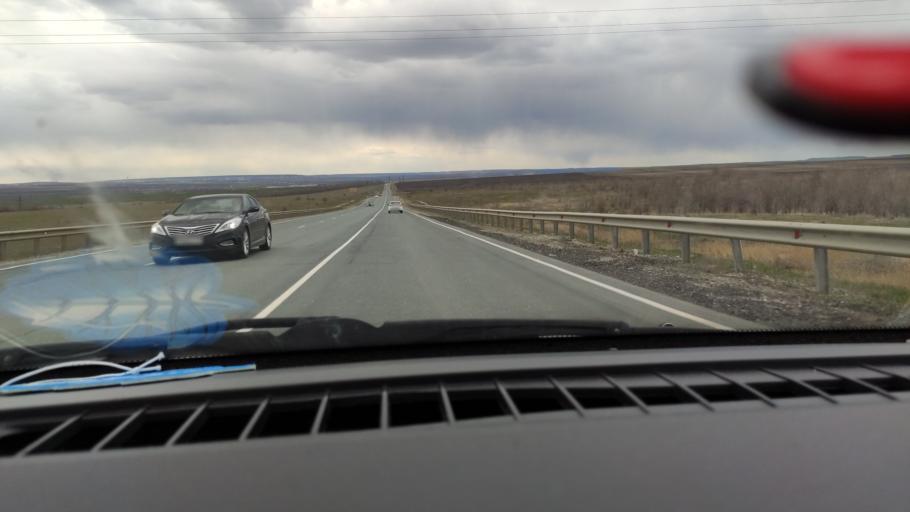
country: RU
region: Saratov
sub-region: Saratovskiy Rayon
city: Saratov
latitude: 51.7602
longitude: 46.0711
